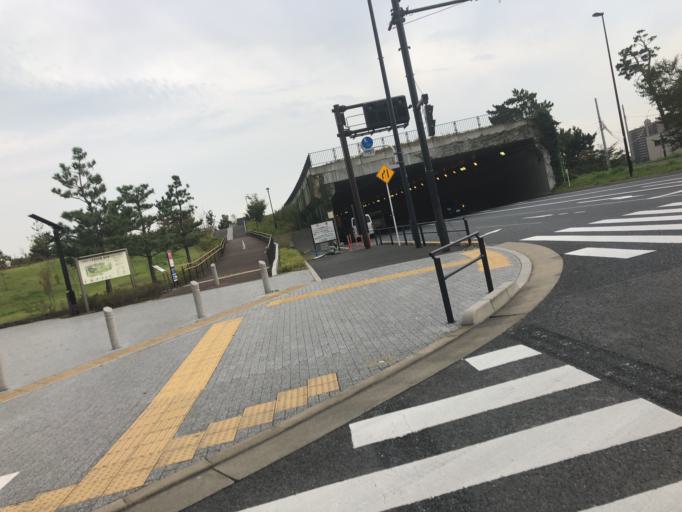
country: JP
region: Tokyo
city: Chofugaoka
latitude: 35.6085
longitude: 139.6314
